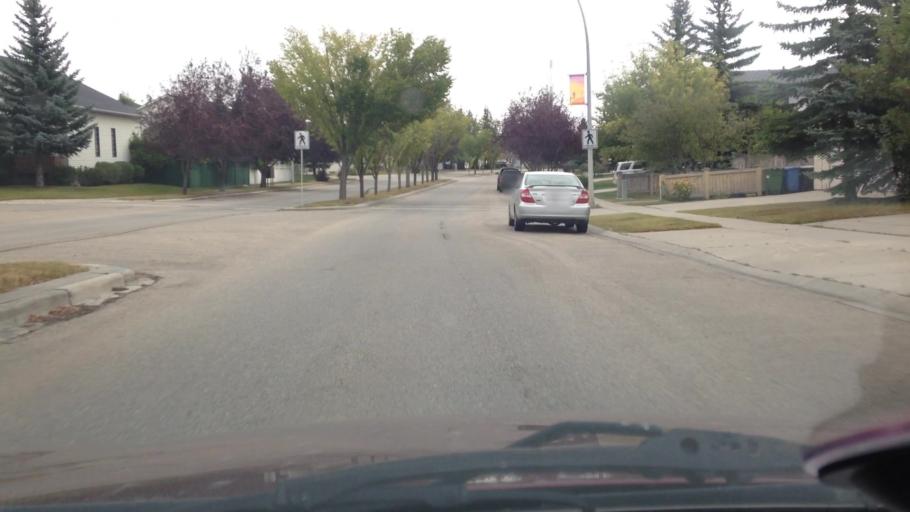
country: CA
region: Alberta
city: Calgary
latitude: 51.1472
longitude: -114.1110
